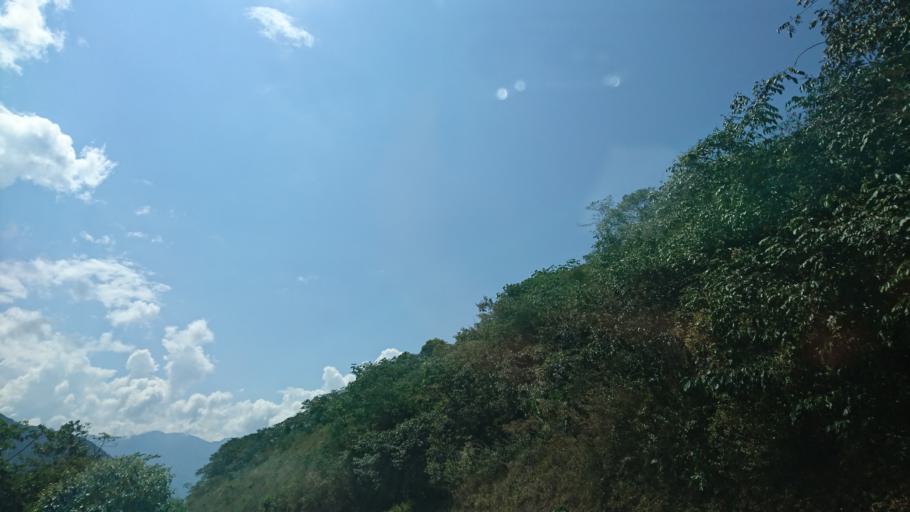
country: BO
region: La Paz
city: Coroico
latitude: -16.2067
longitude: -67.7817
